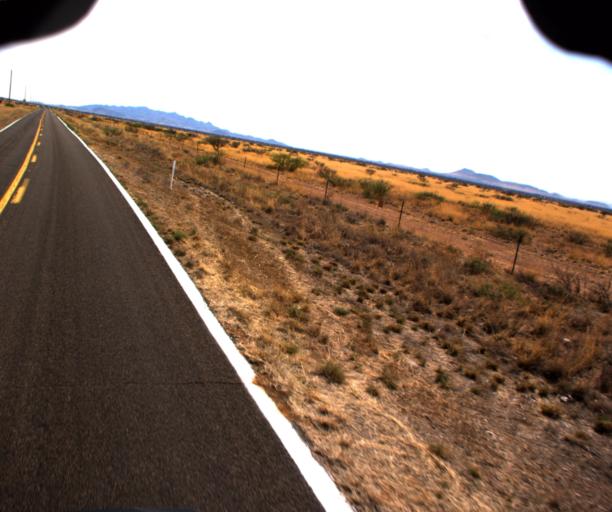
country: US
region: Arizona
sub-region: Cochise County
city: Willcox
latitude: 31.9335
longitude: -109.4914
